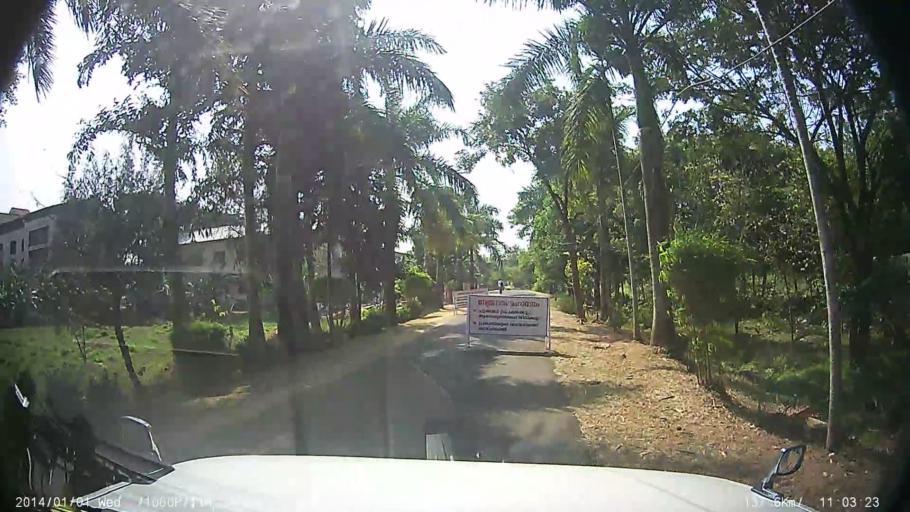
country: IN
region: Kerala
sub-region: Palakkad district
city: Palakkad
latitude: 10.7390
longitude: 76.6501
